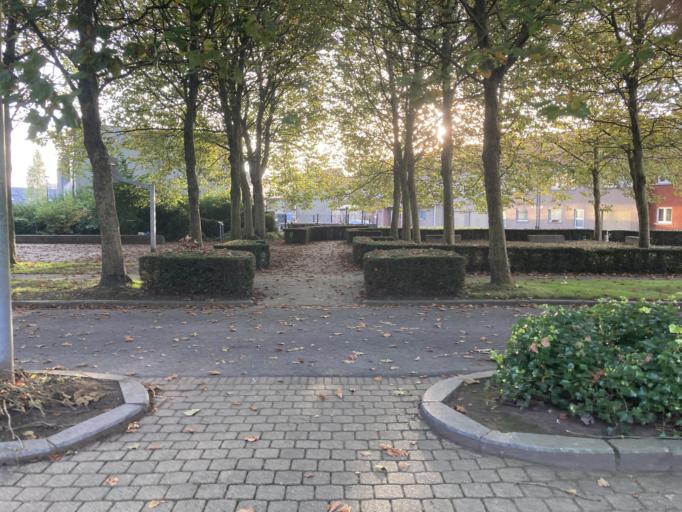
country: BE
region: Flanders
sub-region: Provincie West-Vlaanderen
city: Wervik
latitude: 50.7838
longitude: 3.0319
